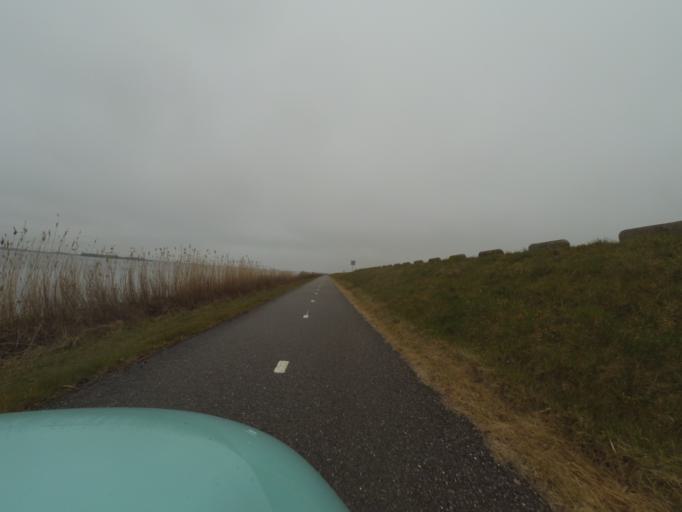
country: NL
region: Flevoland
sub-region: Gemeente Dronten
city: Biddinghuizen
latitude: 52.4120
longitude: 5.7073
